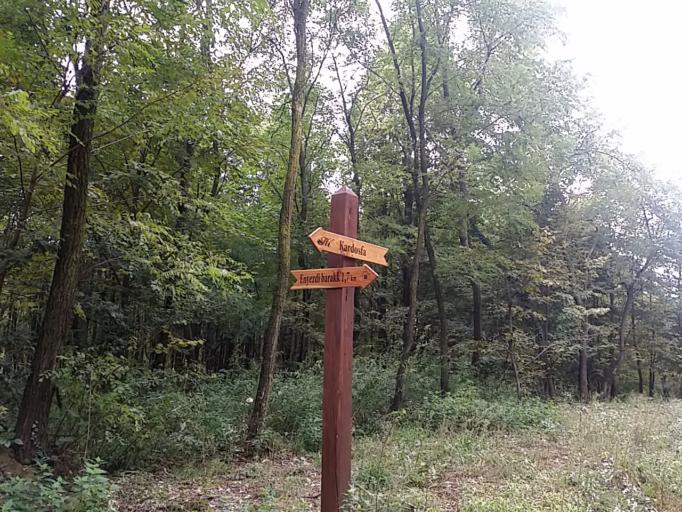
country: HU
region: Somogy
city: Kaposvar
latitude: 46.2248
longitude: 17.7704
